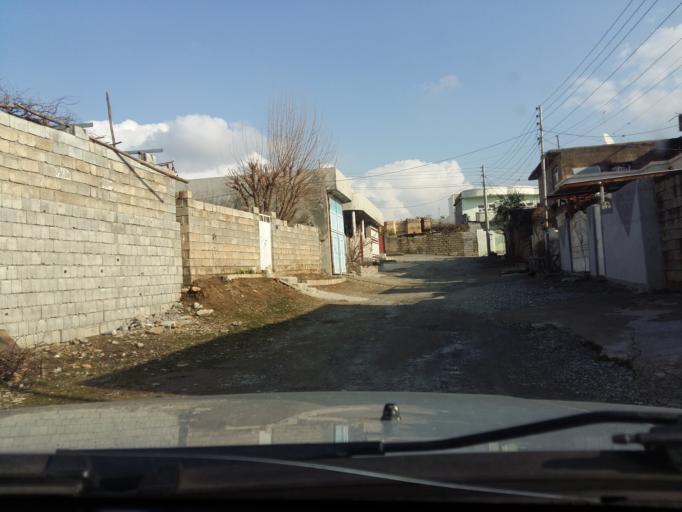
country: IQ
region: As Sulaymaniyah
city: Qeladize
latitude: 36.1784
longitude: 45.1357
